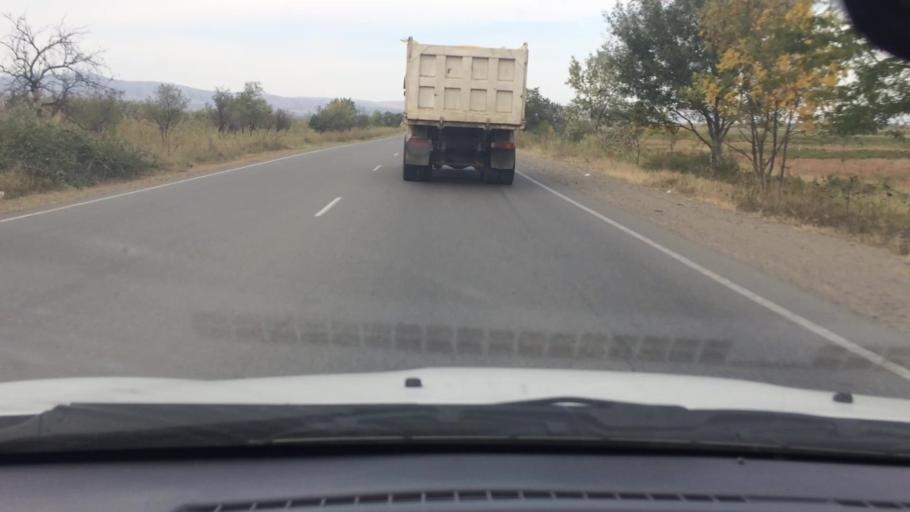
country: GE
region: Kvemo Kartli
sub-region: Marneuli
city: Marneuli
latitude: 41.5273
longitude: 44.7771
